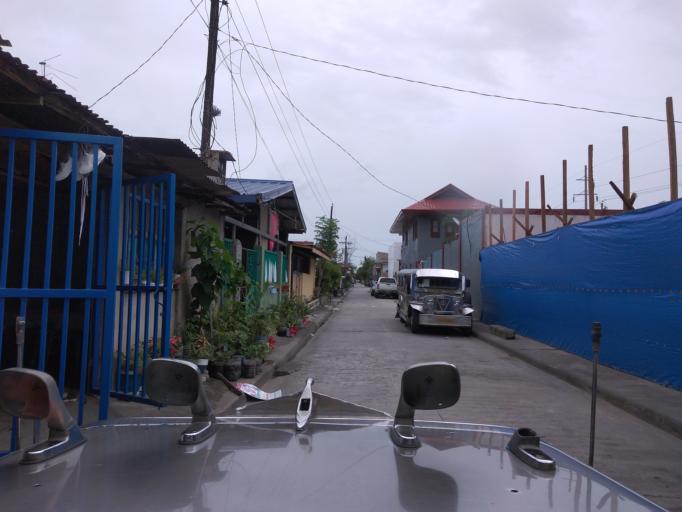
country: PH
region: Central Luzon
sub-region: Province of Pampanga
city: Pandacaqui
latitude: 15.1789
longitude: 120.6522
